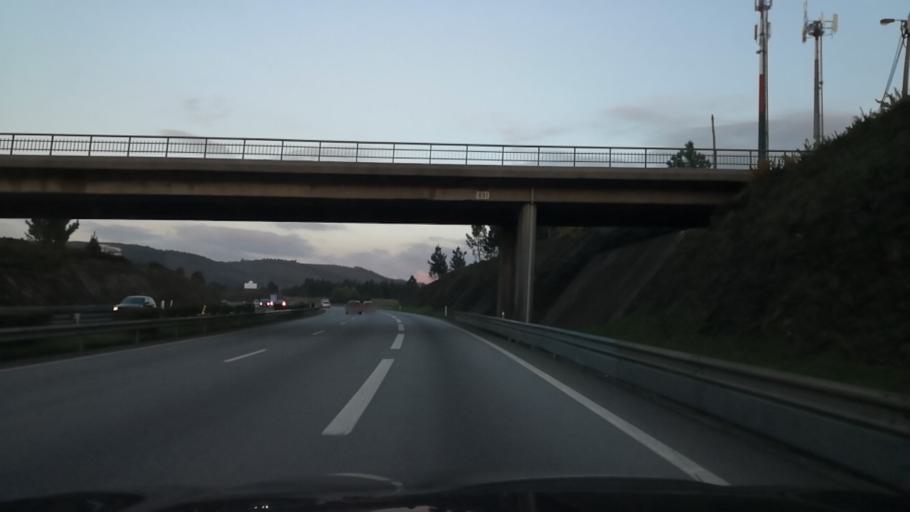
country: PT
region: Porto
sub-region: Paredes
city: Recarei
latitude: 41.1722
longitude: -8.4297
